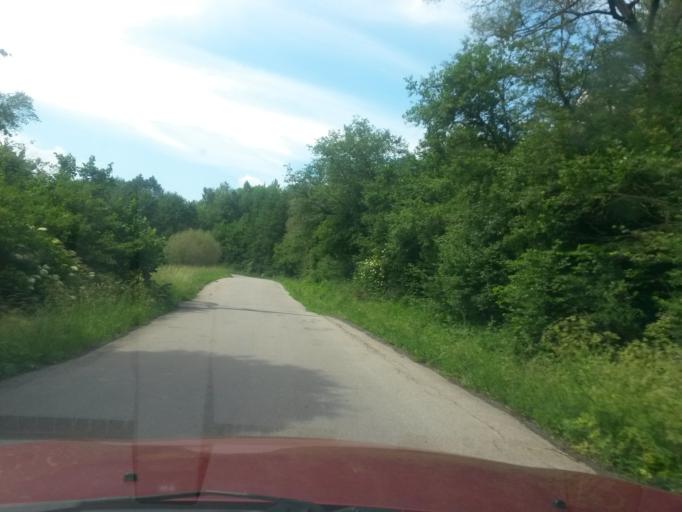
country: UA
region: Zakarpattia
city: Velykyi Bereznyi
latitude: 48.9165
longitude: 22.3718
